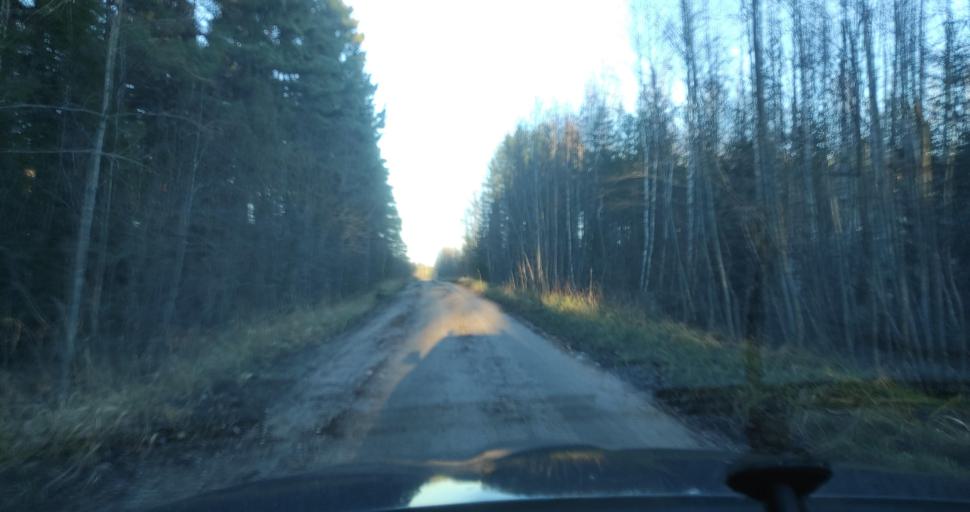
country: LV
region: Dundaga
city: Dundaga
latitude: 57.3826
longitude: 22.0814
